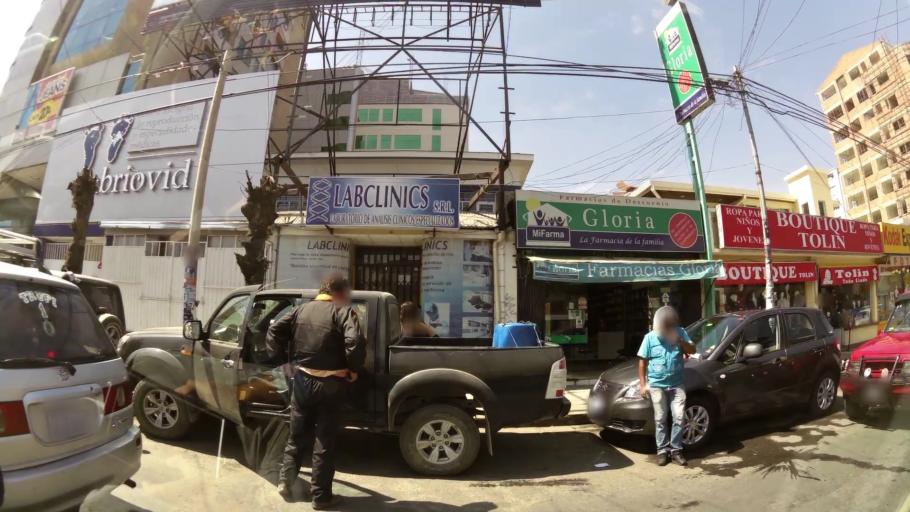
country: BO
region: La Paz
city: La Paz
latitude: -16.5406
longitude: -68.0776
